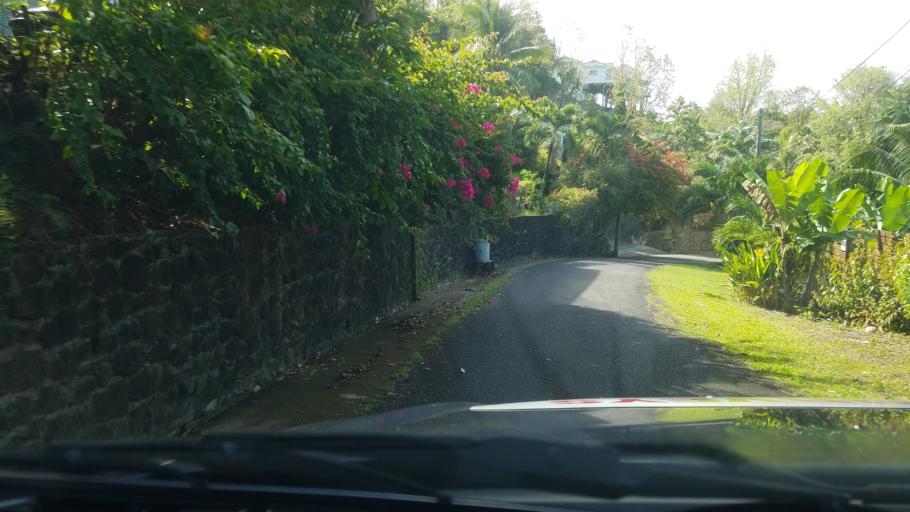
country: LC
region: Castries Quarter
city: Castries
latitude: 14.0216
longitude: -61.0025
